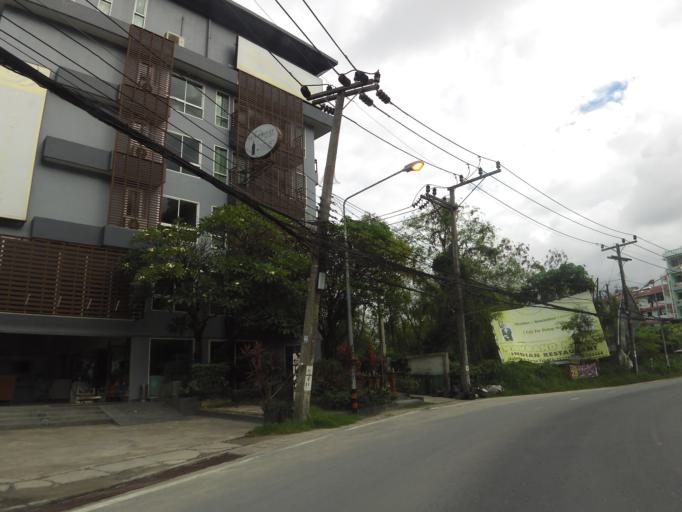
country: TH
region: Phuket
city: Patong
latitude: 7.8774
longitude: 98.2904
